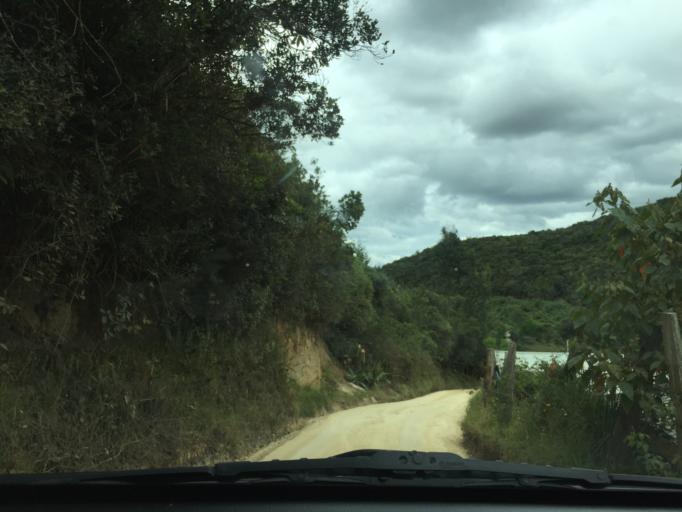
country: CO
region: Cundinamarca
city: Tabio
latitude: 4.9200
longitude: -74.1104
